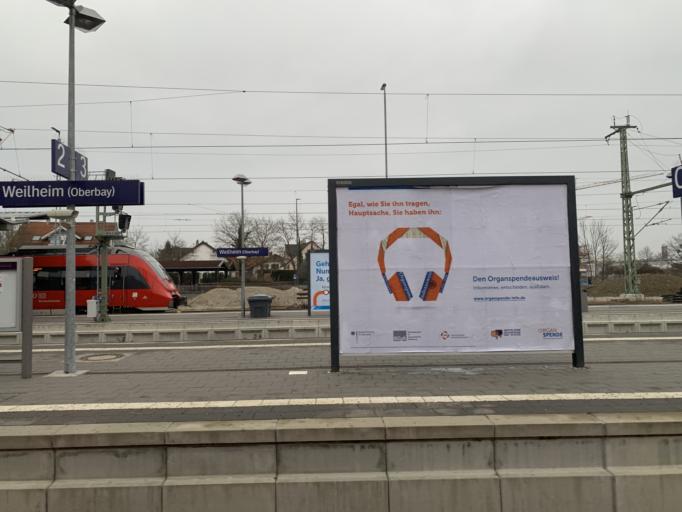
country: DE
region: Bavaria
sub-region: Upper Bavaria
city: Weilheim
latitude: 47.8457
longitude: 11.1435
